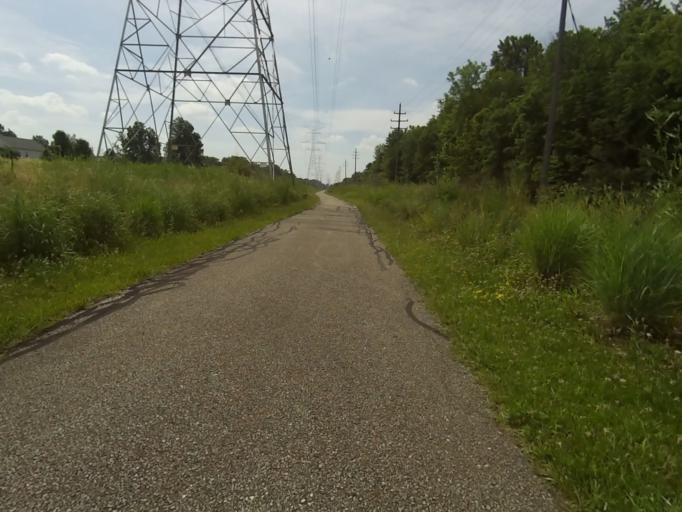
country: US
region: Ohio
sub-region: Summit County
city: Northfield
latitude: 41.3186
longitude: -81.5666
